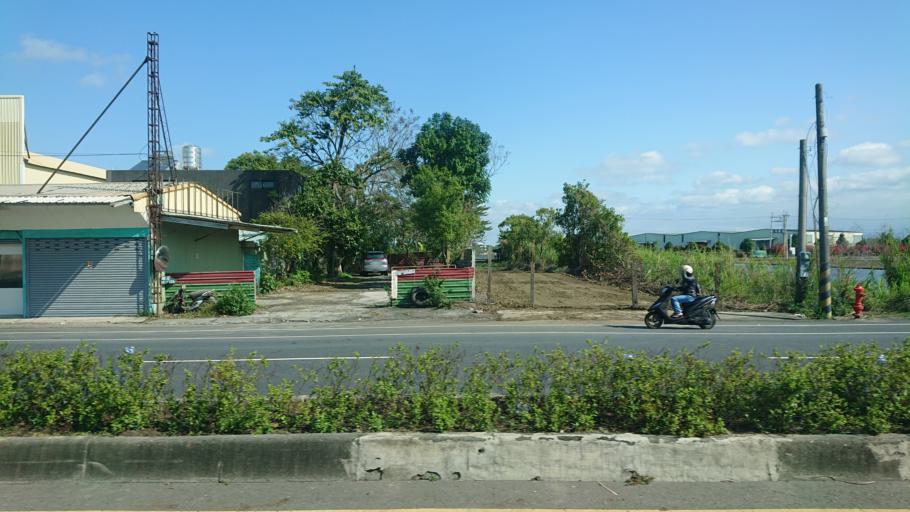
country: TW
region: Taiwan
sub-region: Chiayi
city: Taibao
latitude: 23.4362
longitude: 120.3907
